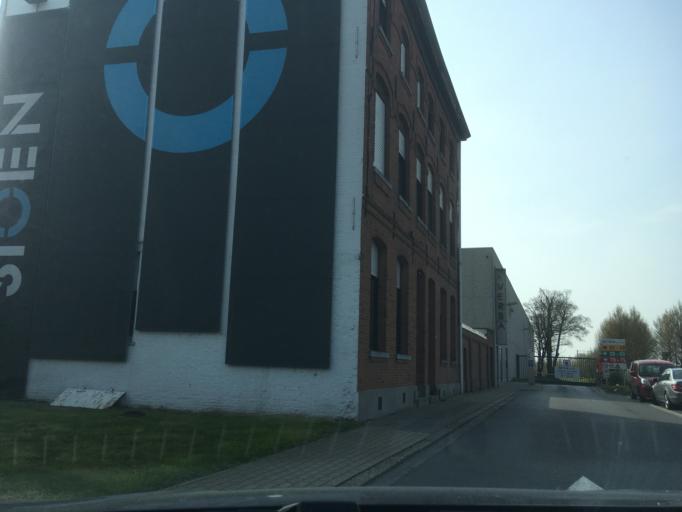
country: BE
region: Flanders
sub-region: Provincie West-Vlaanderen
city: Ardooie
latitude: 50.9897
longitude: 3.1996
